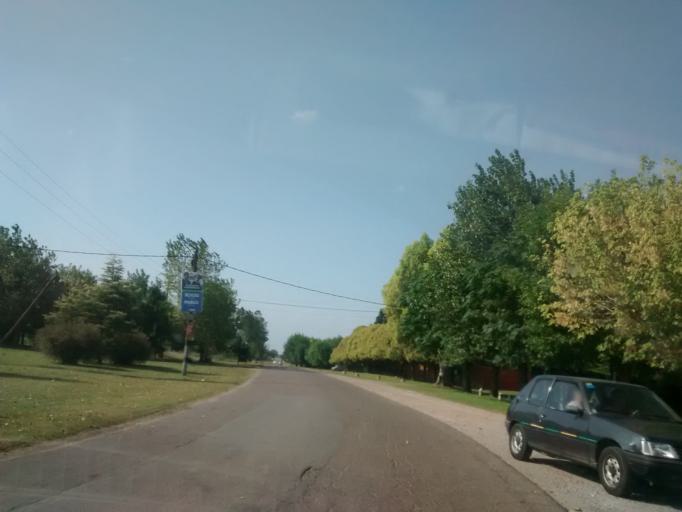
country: AR
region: Buenos Aires
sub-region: Partido de La Plata
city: La Plata
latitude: -35.0030
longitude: -57.8994
